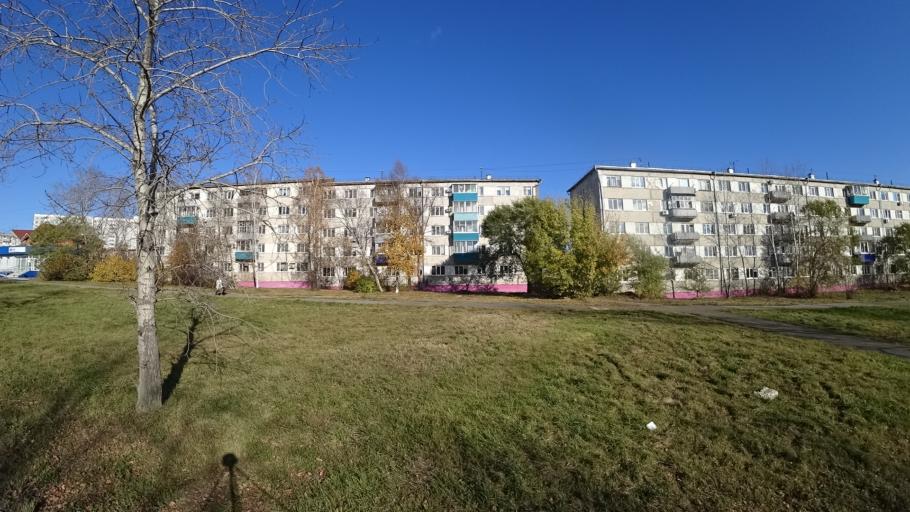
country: RU
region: Khabarovsk Krai
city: Amursk
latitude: 50.2361
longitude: 136.9112
